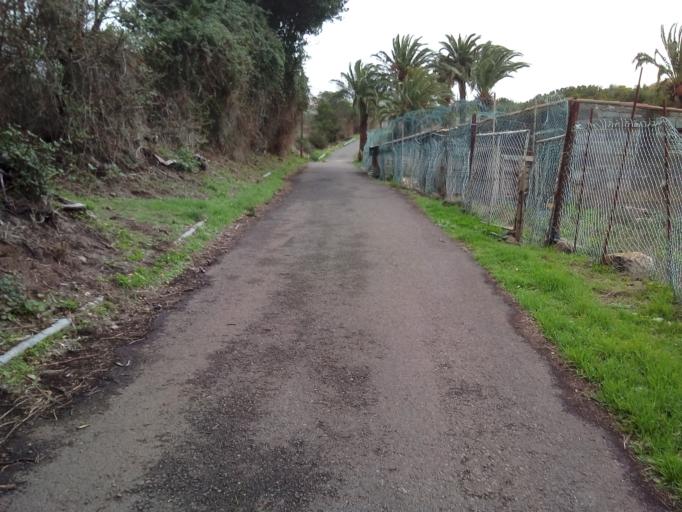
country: ES
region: Canary Islands
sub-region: Provincia de Santa Cruz de Tenerife
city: Vallehermosa
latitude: 28.1324
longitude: -17.2940
